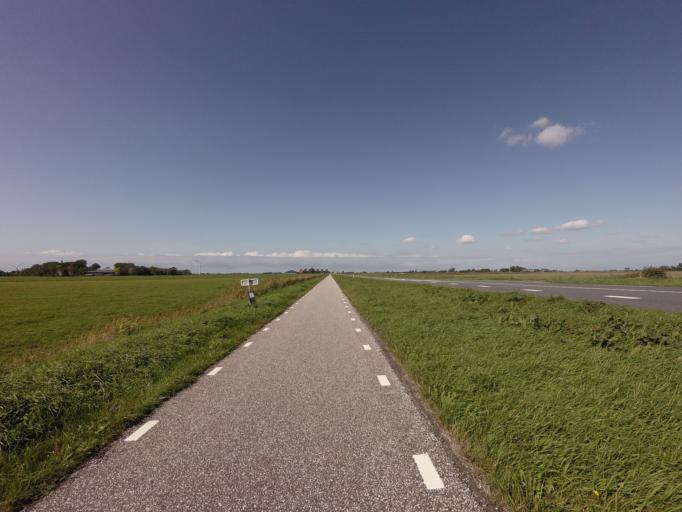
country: NL
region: Friesland
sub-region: Gemeente Littenseradiel
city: Makkum
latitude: 53.1109
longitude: 5.6863
